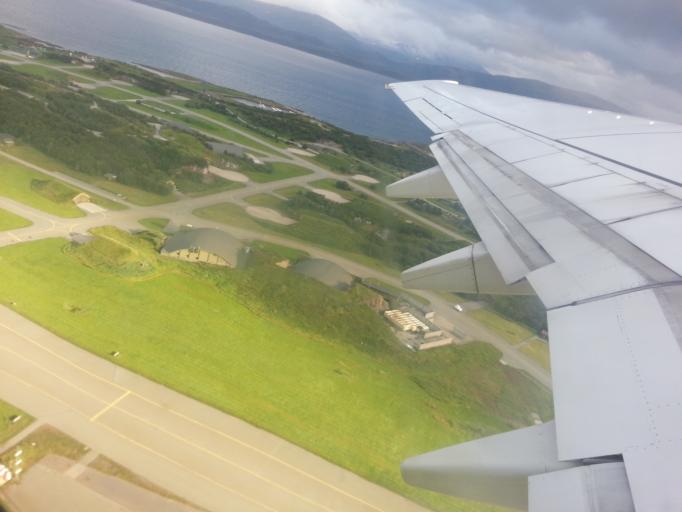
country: NO
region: Nordland
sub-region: Bodo
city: Bodo
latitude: 67.2670
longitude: 14.3387
